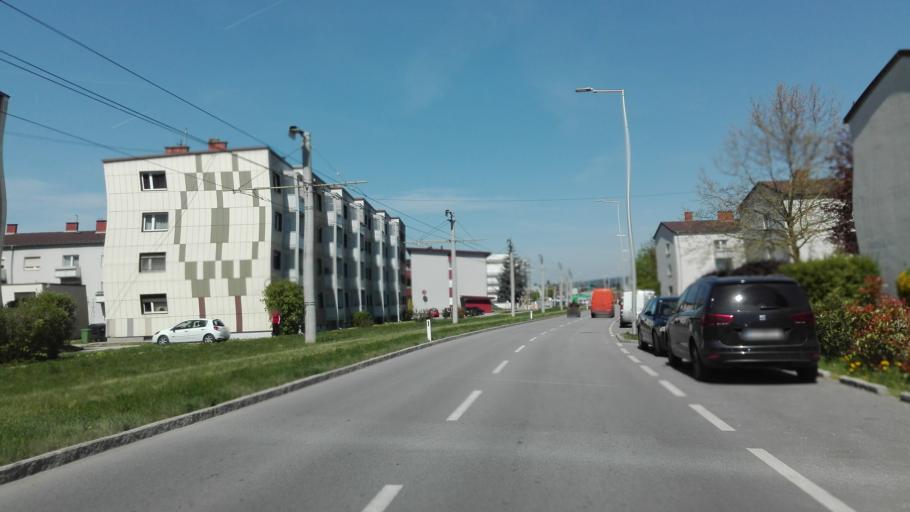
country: AT
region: Upper Austria
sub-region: Politischer Bezirk Linz-Land
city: Traun
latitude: 48.2238
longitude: 14.2353
